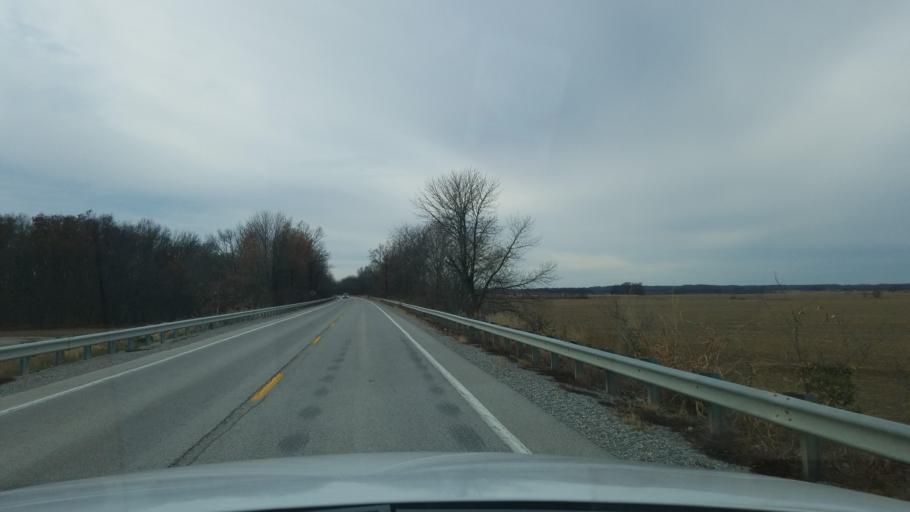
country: US
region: Illinois
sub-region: White County
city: Carmi
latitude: 37.9375
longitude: -88.0762
